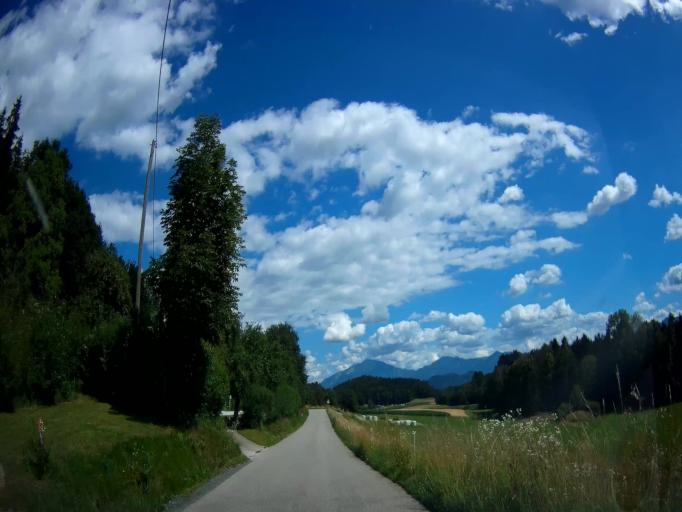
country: AT
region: Carinthia
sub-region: Politischer Bezirk Klagenfurt Land
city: Poggersdorf
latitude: 46.6602
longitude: 14.5399
